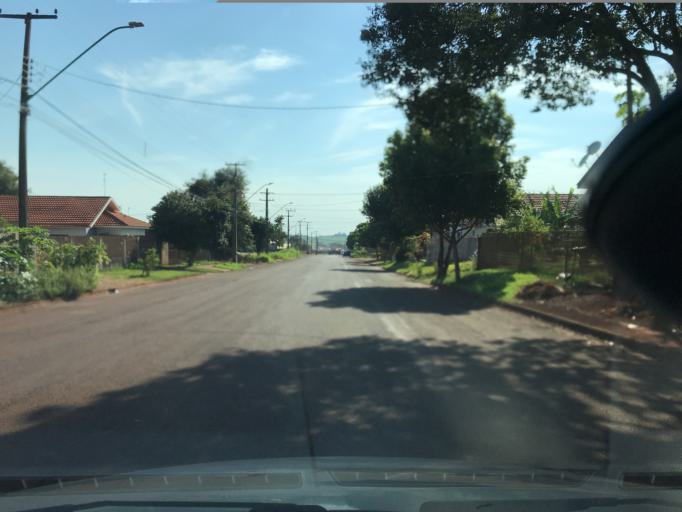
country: BR
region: Parana
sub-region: Palotina
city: Palotina
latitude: -24.2954
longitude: -53.8334
